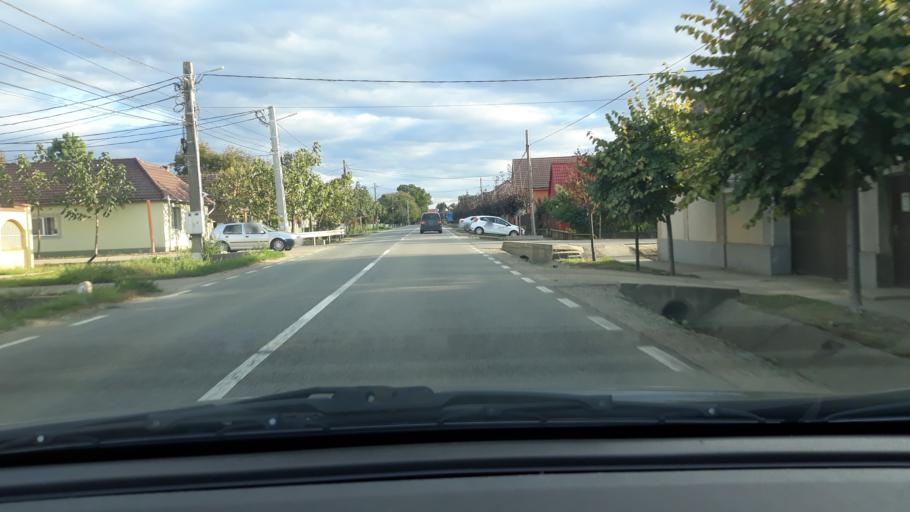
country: RO
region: Bihor
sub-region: Comuna Biharea
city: Biharea
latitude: 47.1614
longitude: 21.9223
